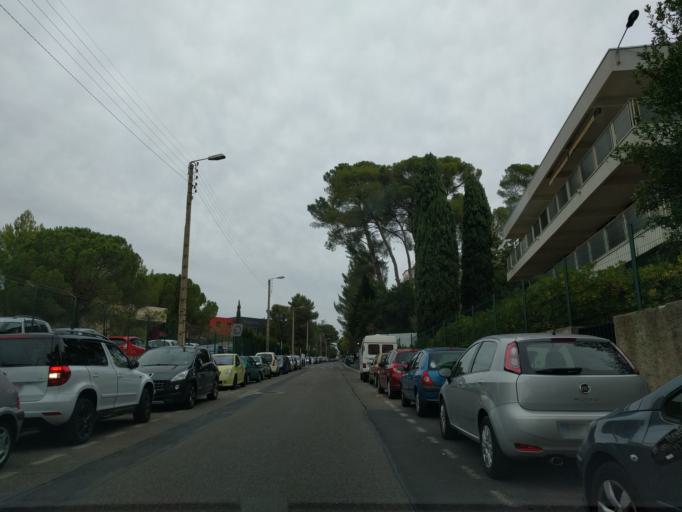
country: FR
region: Languedoc-Roussillon
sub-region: Departement de l'Herault
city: Montpellier
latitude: 43.6311
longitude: 3.8711
